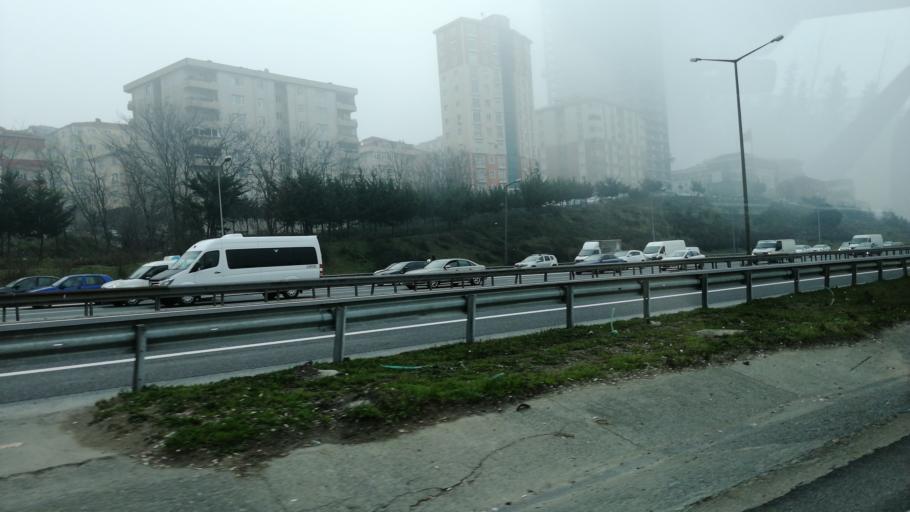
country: TR
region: Istanbul
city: Umraniye
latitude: 41.0040
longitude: 29.1207
